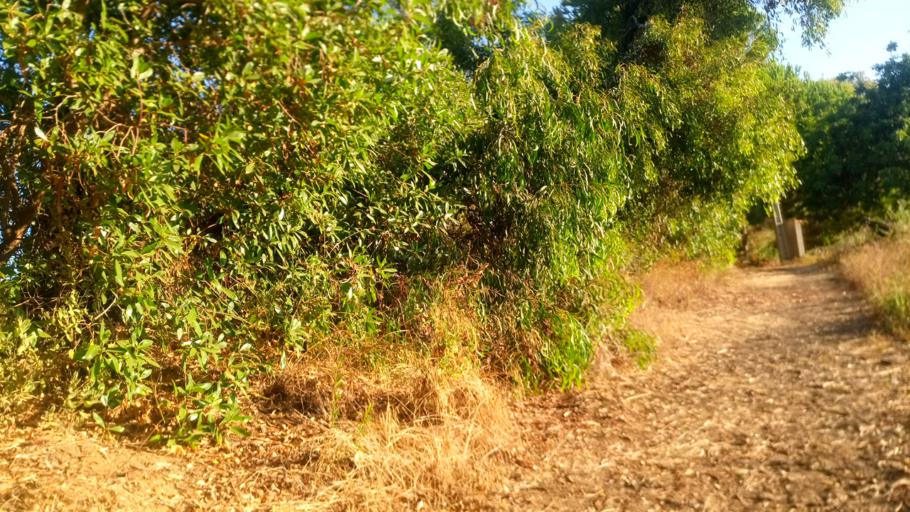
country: PT
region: Faro
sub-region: Tavira
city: Tavira
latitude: 37.1432
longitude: -7.5823
